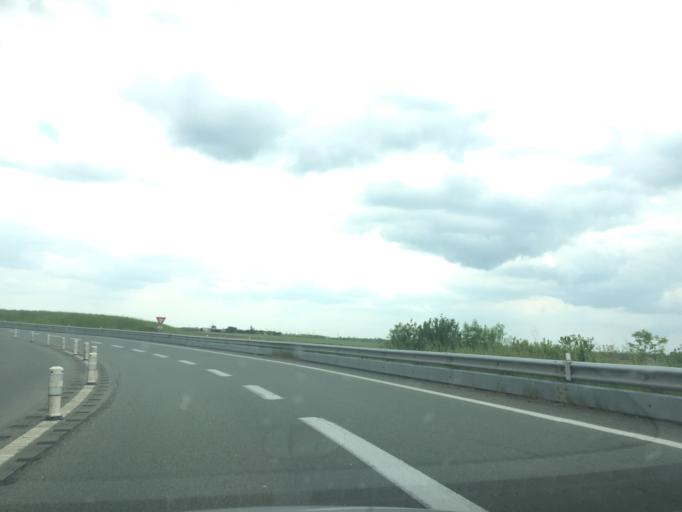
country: FR
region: Pays de la Loire
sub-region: Departement de la Vendee
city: Benet
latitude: 46.3888
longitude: -0.6565
